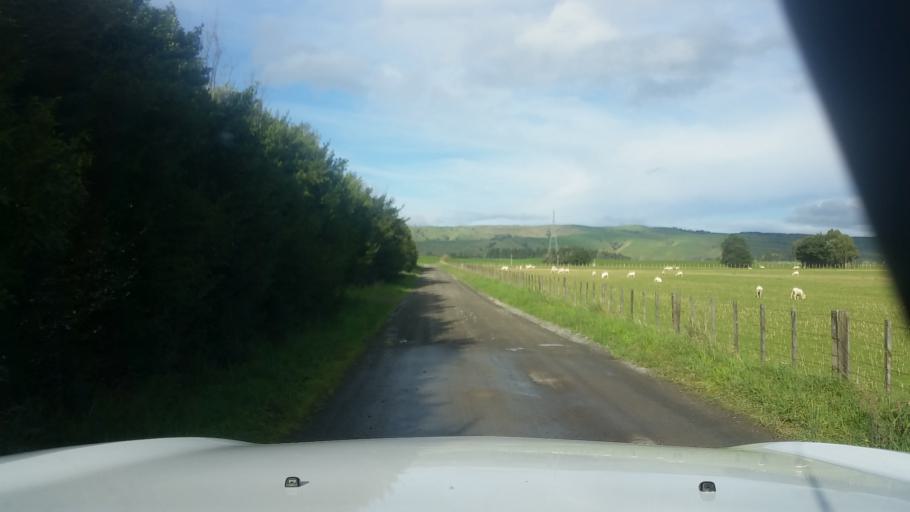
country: NZ
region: Wellington
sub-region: Masterton District
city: Masterton
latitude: -41.1023
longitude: 175.4656
